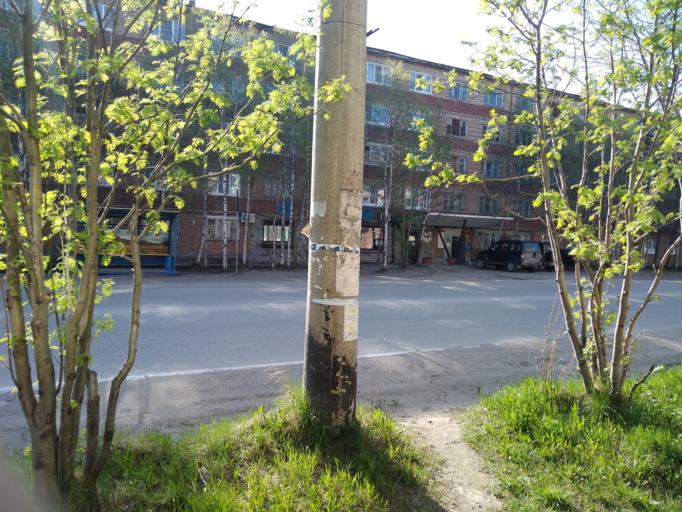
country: RU
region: Komi Republic
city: Pechora
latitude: 65.1265
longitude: 57.1543
